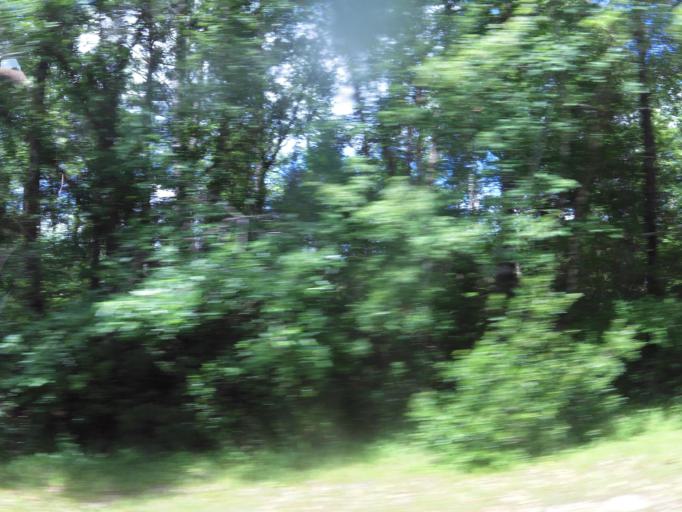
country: US
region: Florida
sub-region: Clay County
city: Asbury Lake
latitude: 29.9120
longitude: -81.8870
